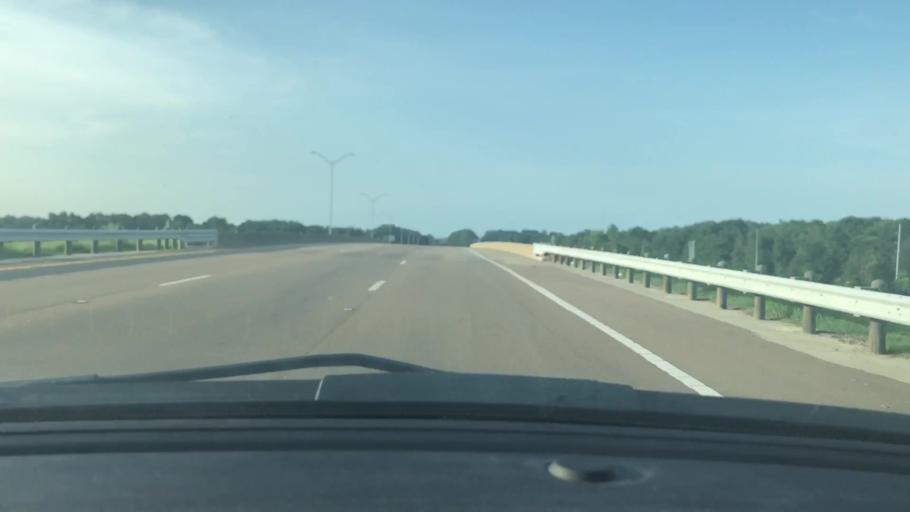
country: US
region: Texas
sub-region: Bowie County
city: Wake Village
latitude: 33.4018
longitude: -94.0978
